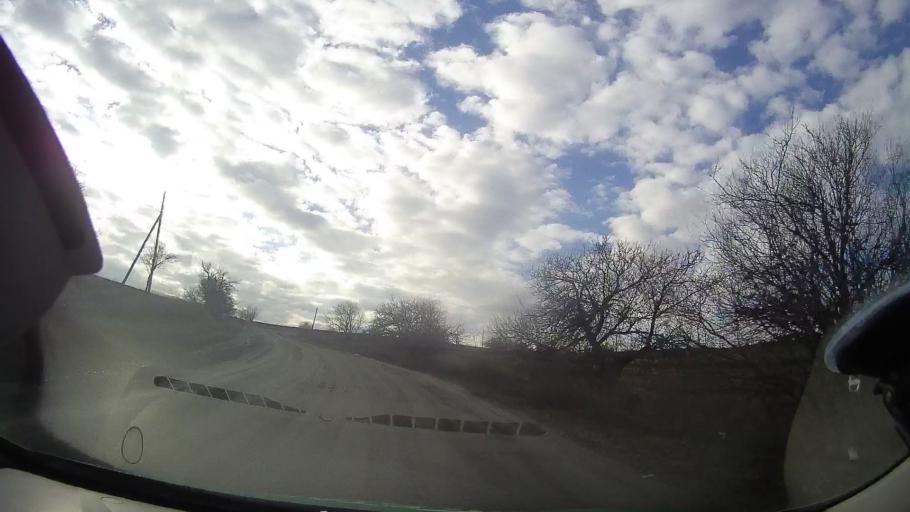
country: RO
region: Cluj
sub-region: Comuna Savadisla
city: Savadisla
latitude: 46.6402
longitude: 23.4578
